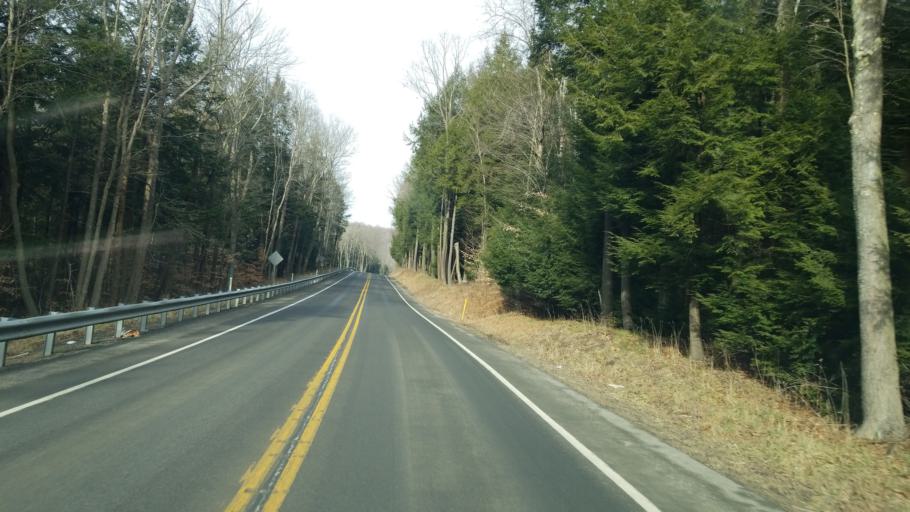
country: US
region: Pennsylvania
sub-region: Indiana County
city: Johnsonburg
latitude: 40.7603
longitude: -78.8662
